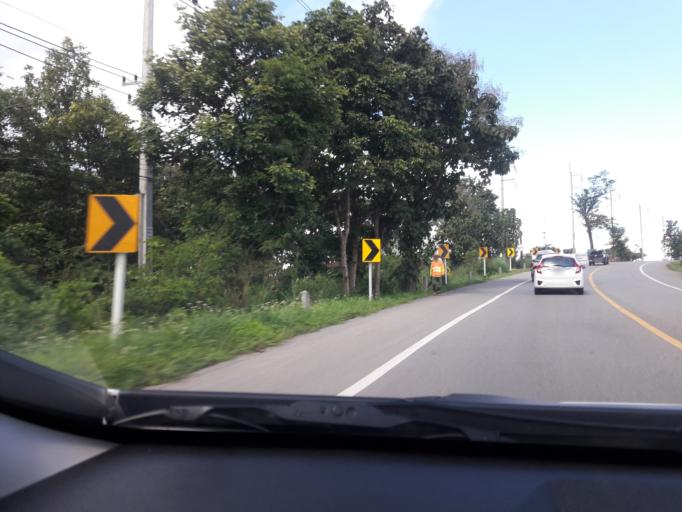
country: TH
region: Mae Hong Son
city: Mae Hi
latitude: 19.3366
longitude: 98.4317
